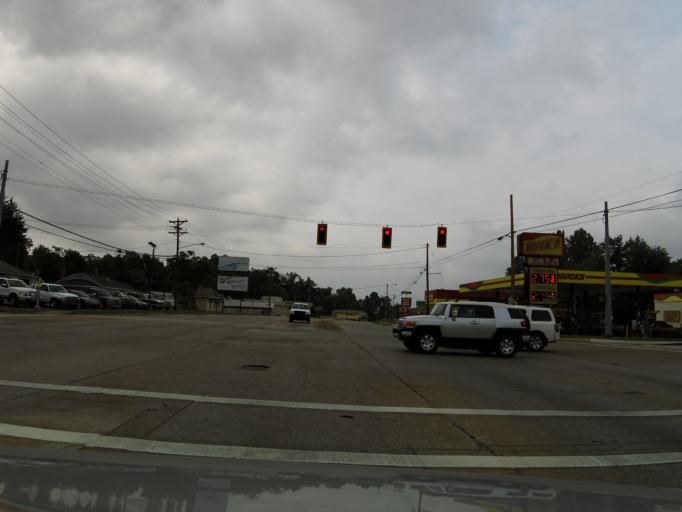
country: US
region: Kentucky
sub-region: Hopkins County
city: Madisonville
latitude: 37.3182
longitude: -87.5005
